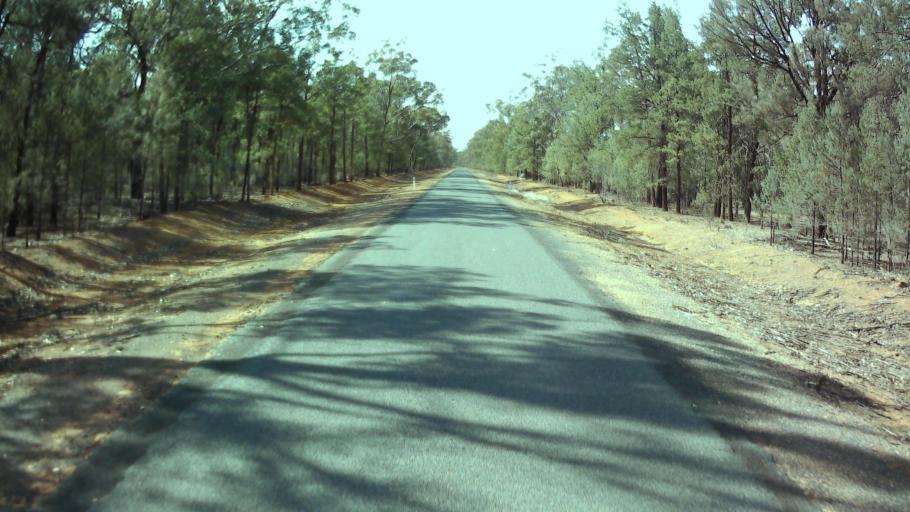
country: AU
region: New South Wales
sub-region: Weddin
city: Grenfell
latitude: -33.7165
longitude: 148.0257
